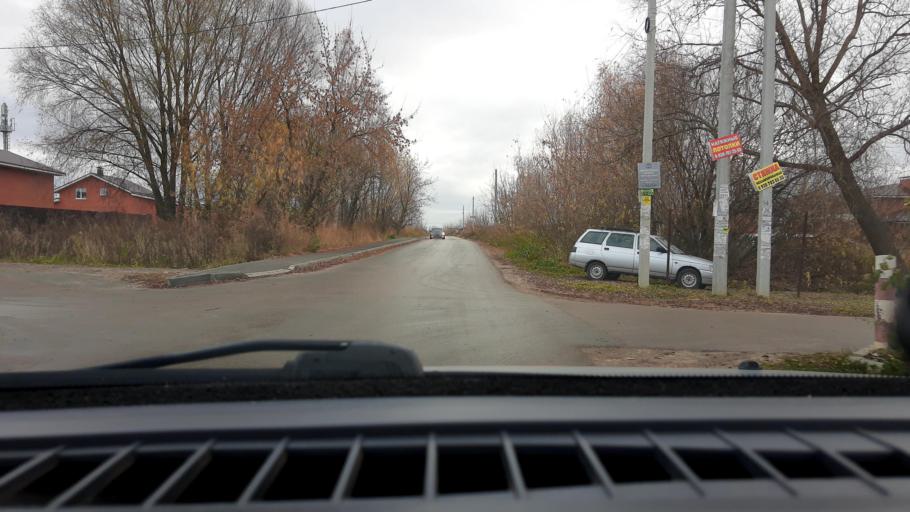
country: RU
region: Nizjnij Novgorod
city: Afonino
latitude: 56.2063
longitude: 44.1262
